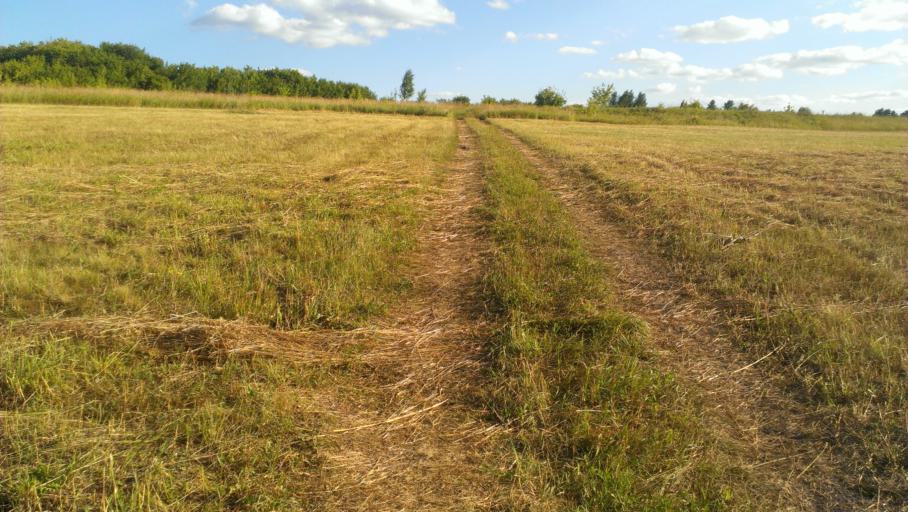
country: RU
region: Altai Krai
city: Gon'ba
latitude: 53.3888
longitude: 83.5991
